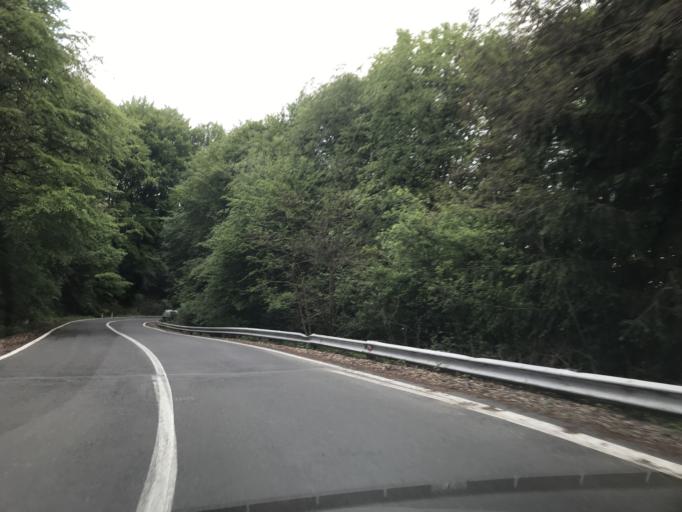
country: RO
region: Sibiu
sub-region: Comuna Cartisoara
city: Cartisoara
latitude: 45.6777
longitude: 24.5900
